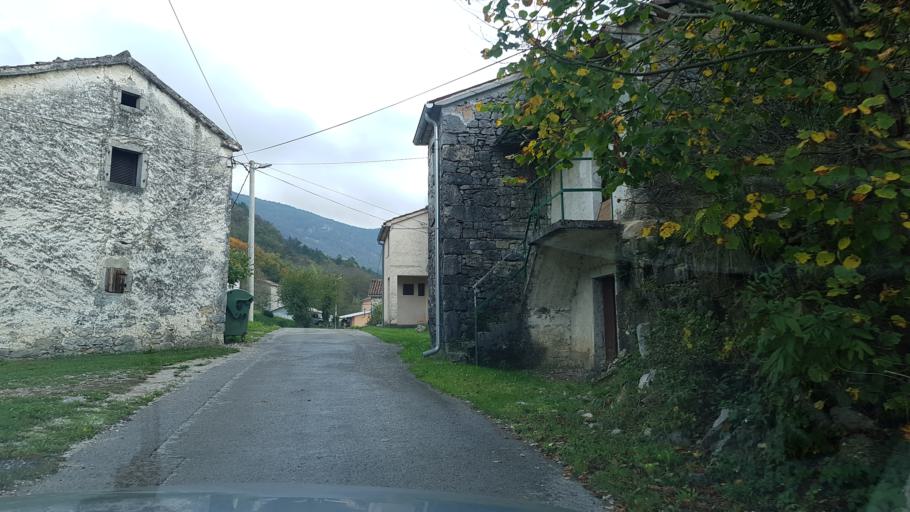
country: HR
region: Istarska
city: Buzet
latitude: 45.4111
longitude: 14.1022
